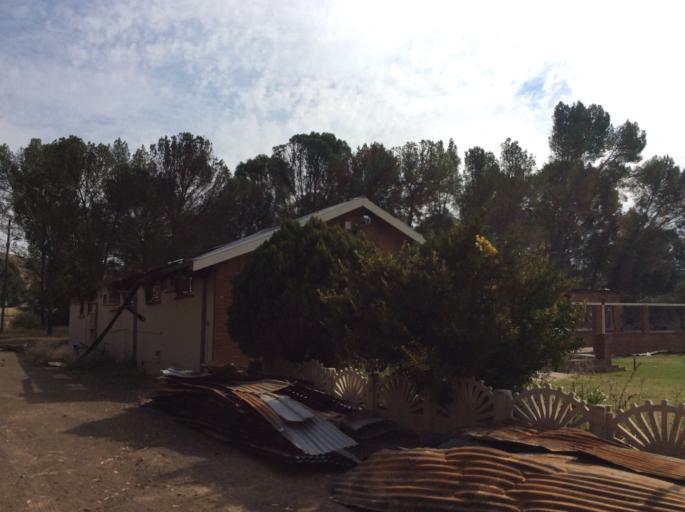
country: ZA
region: Orange Free State
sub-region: Xhariep District Municipality
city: Dewetsdorp
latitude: -29.5767
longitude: 26.6647
